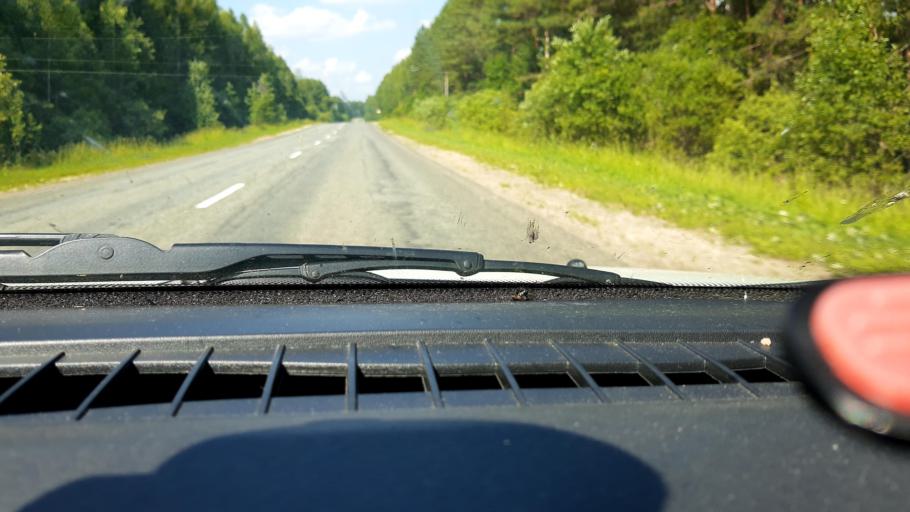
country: RU
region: Nizjnij Novgorod
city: Tonkino
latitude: 57.2895
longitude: 46.4621
